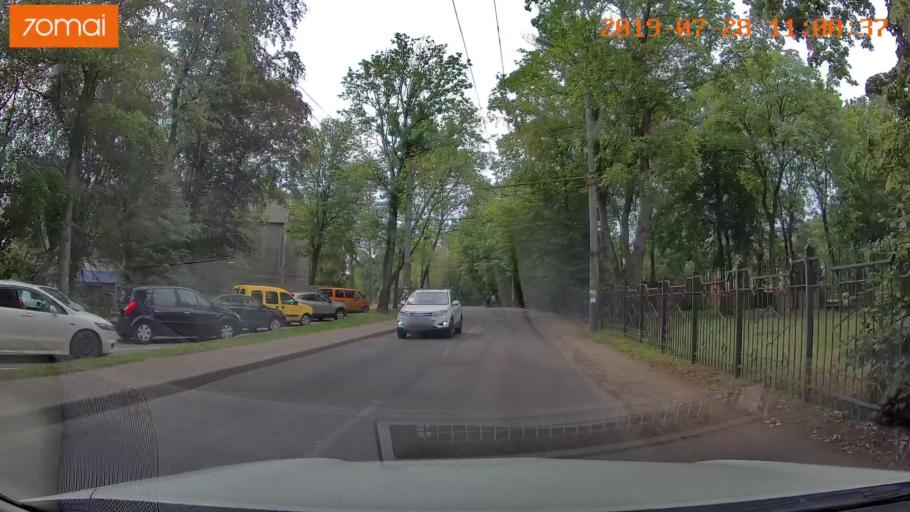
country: RU
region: Kaliningrad
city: Vzmorye
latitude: 54.7262
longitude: 20.3627
